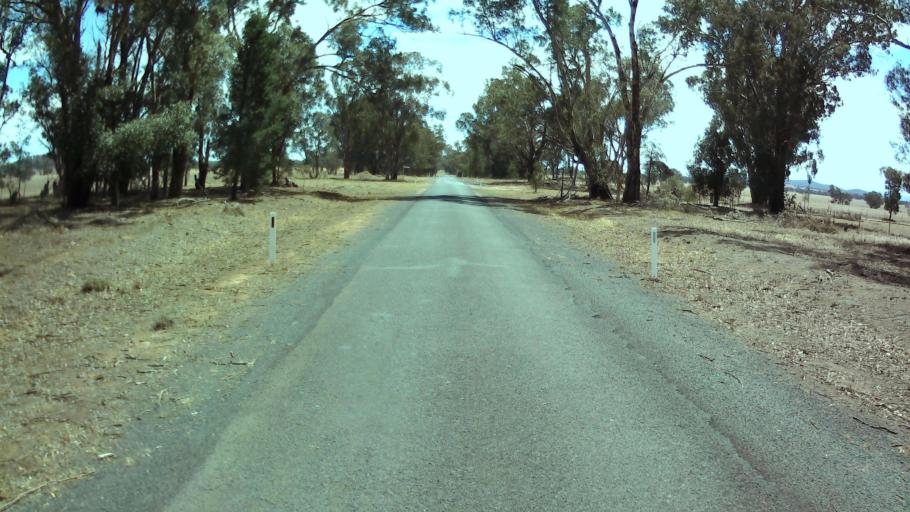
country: AU
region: New South Wales
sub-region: Weddin
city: Grenfell
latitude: -33.7557
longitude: 148.2061
